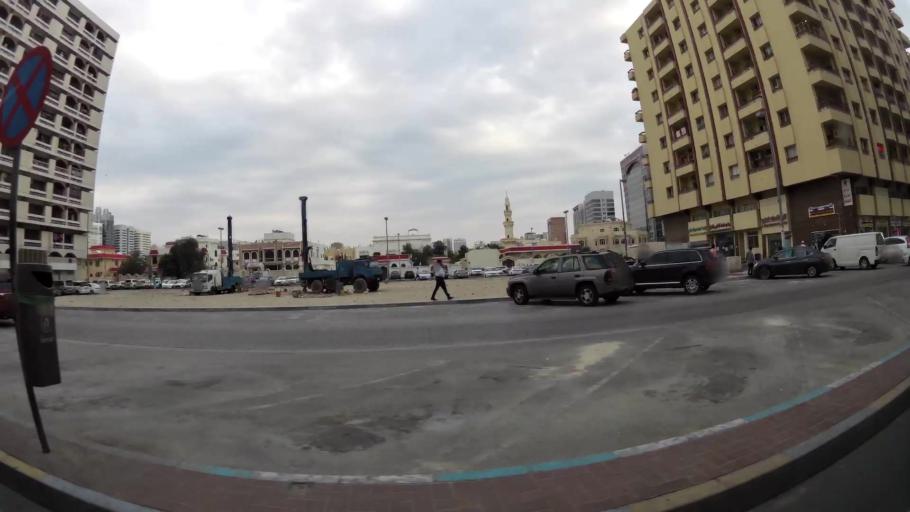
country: AE
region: Abu Dhabi
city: Abu Dhabi
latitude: 24.4880
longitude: 54.3661
